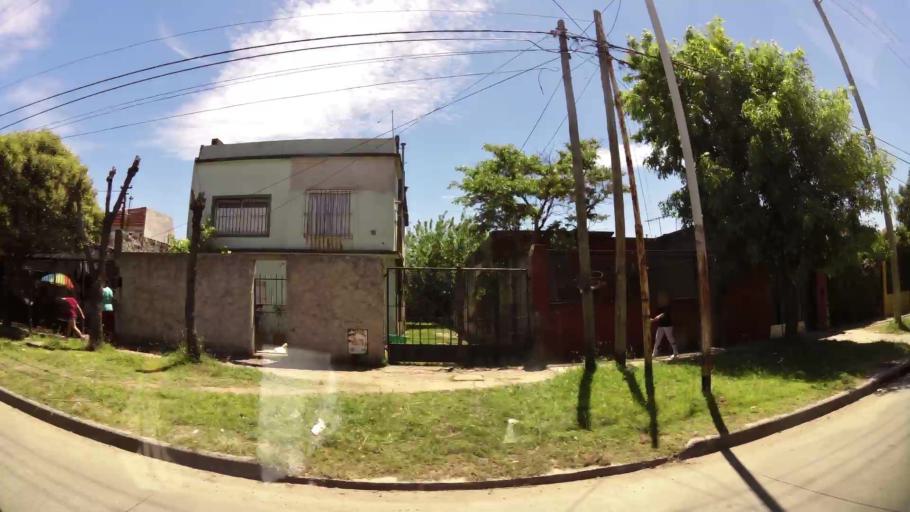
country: AR
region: Buenos Aires
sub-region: Partido de Lanus
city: Lanus
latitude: -34.7241
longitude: -58.3301
